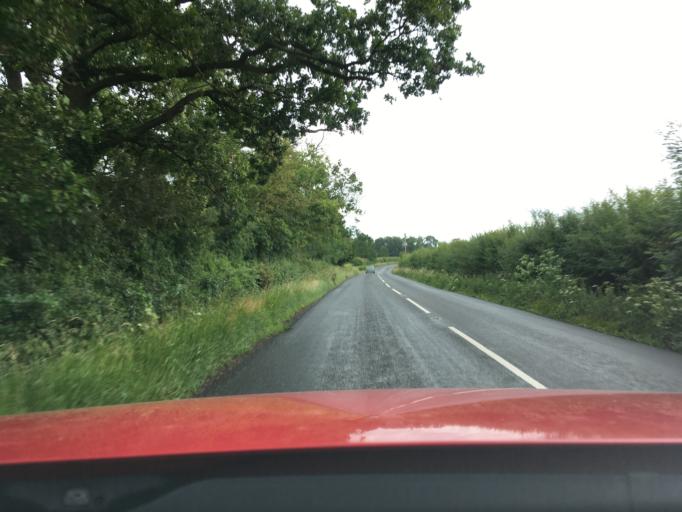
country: GB
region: England
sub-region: Gloucestershire
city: Winchcombe
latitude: 52.0095
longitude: -1.9575
